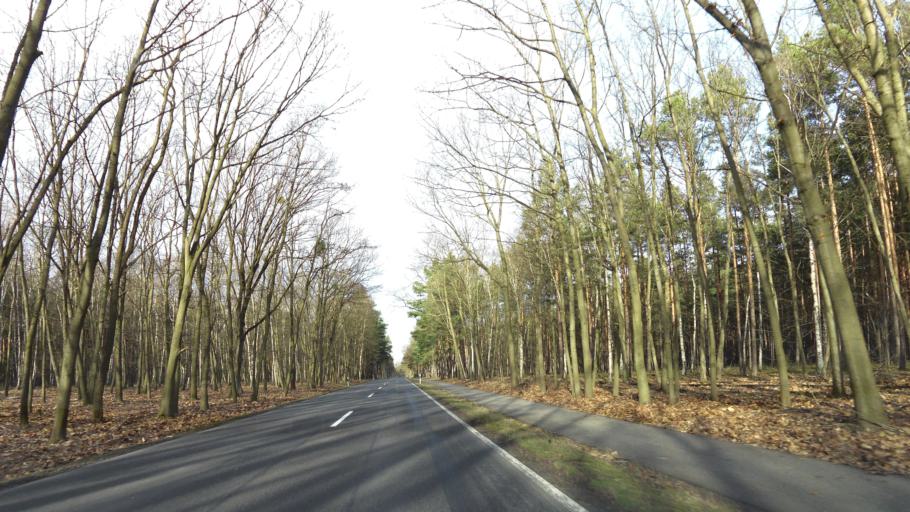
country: DE
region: Brandenburg
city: Michendorf
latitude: 52.3365
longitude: 13.0154
